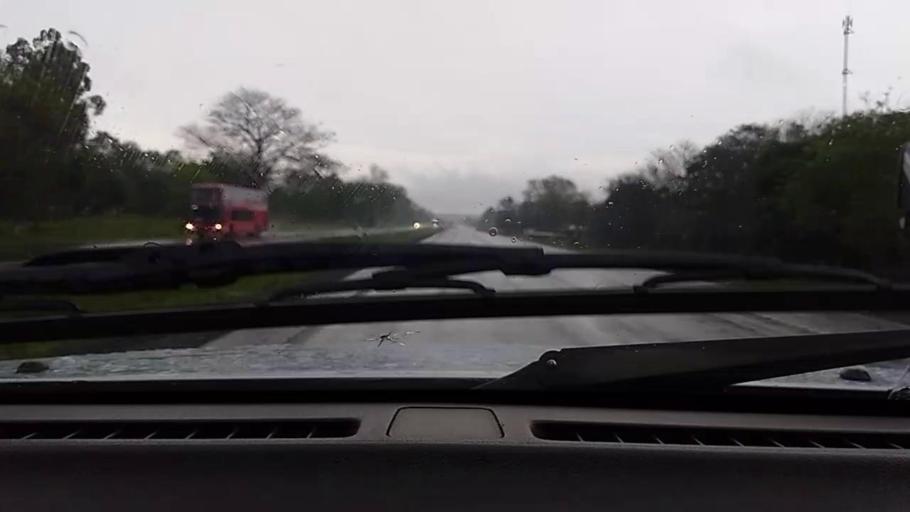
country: PY
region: Caaguazu
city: Repatriacion
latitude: -25.4584
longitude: -55.9195
